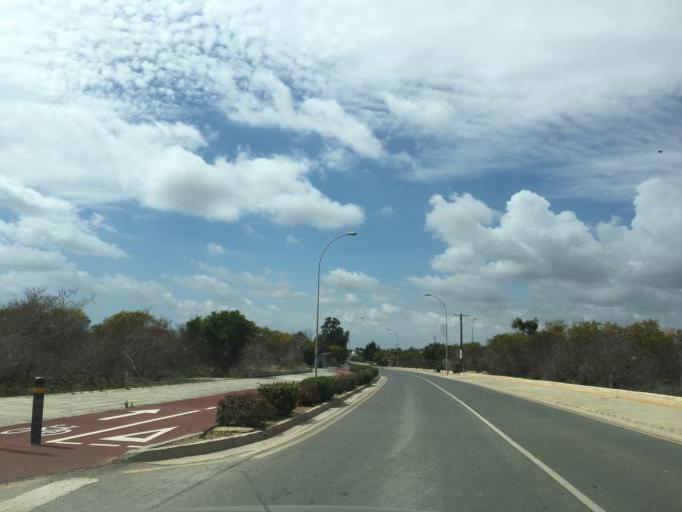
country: CY
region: Ammochostos
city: Ayia Napa
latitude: 34.9889
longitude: 33.9620
